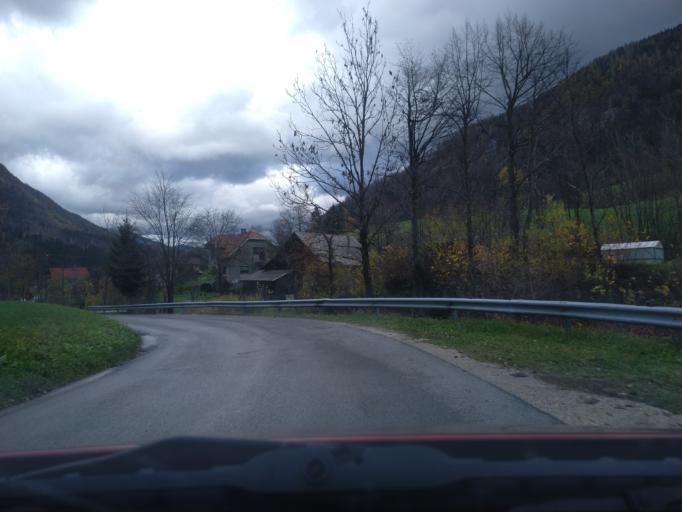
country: SI
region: Luce
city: Luce
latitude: 46.3123
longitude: 14.7014
